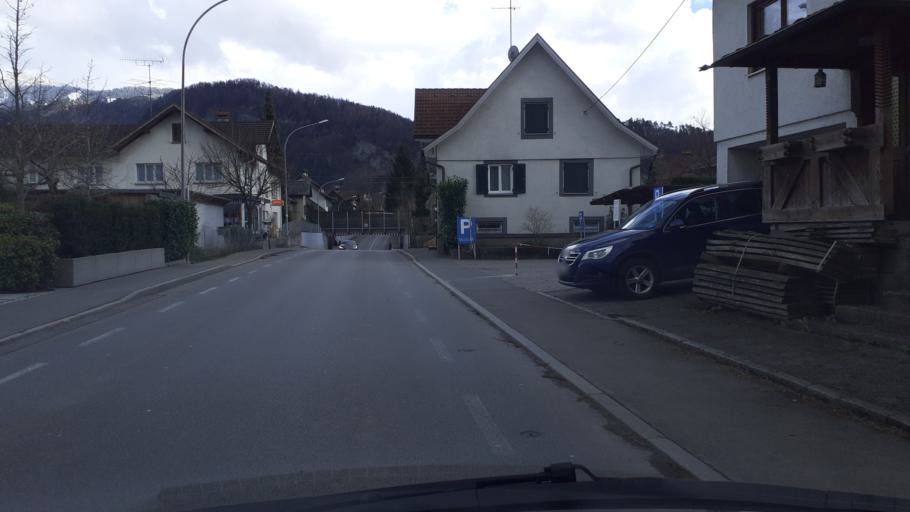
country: AT
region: Vorarlberg
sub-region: Politischer Bezirk Feldkirch
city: Gotzis
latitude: 47.3335
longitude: 9.6322
